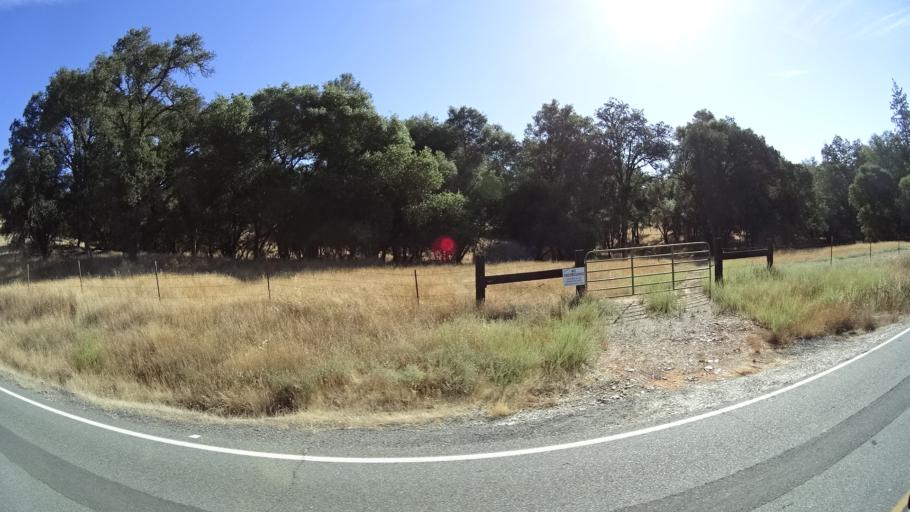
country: US
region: California
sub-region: Calaveras County
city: San Andreas
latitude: 38.1805
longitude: -120.6535
